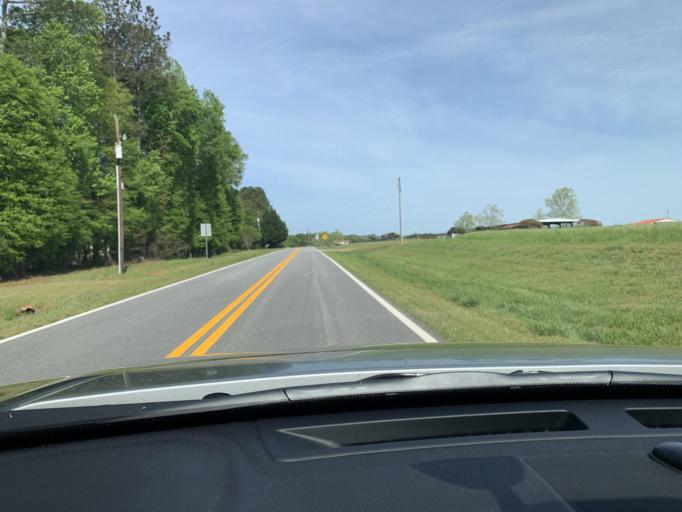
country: US
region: Georgia
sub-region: Oconee County
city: Watkinsville
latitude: 33.8161
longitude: -83.4270
